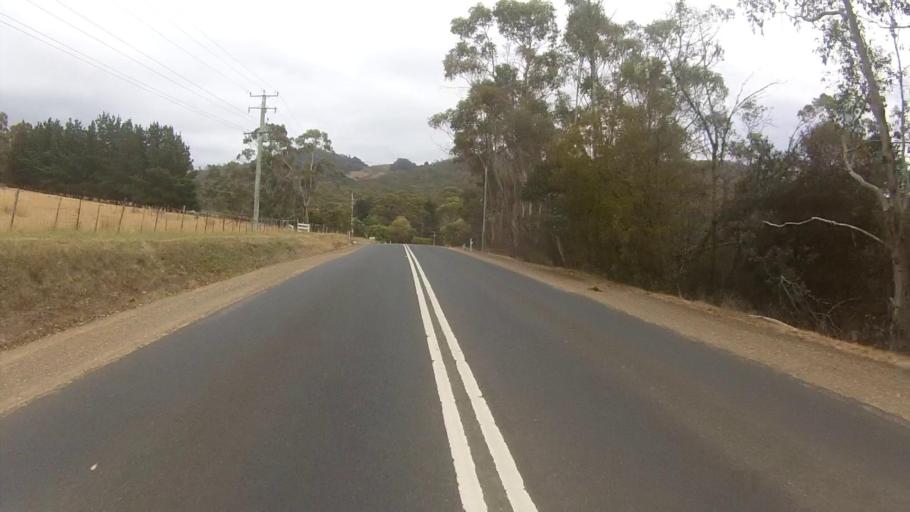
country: AU
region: Tasmania
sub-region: Kingborough
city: Margate
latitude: -43.0141
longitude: 147.2476
